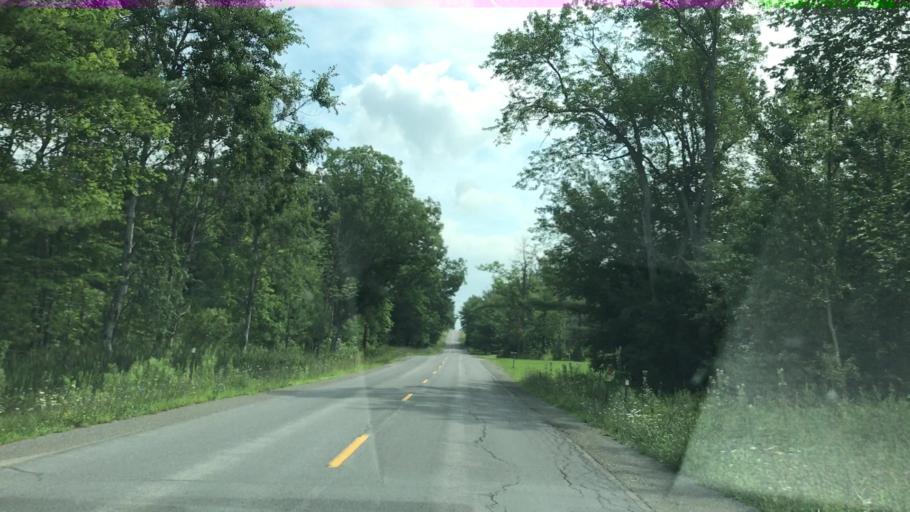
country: US
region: New York
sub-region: Steuben County
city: Sylvan Beach
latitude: 42.5114
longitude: -77.2322
